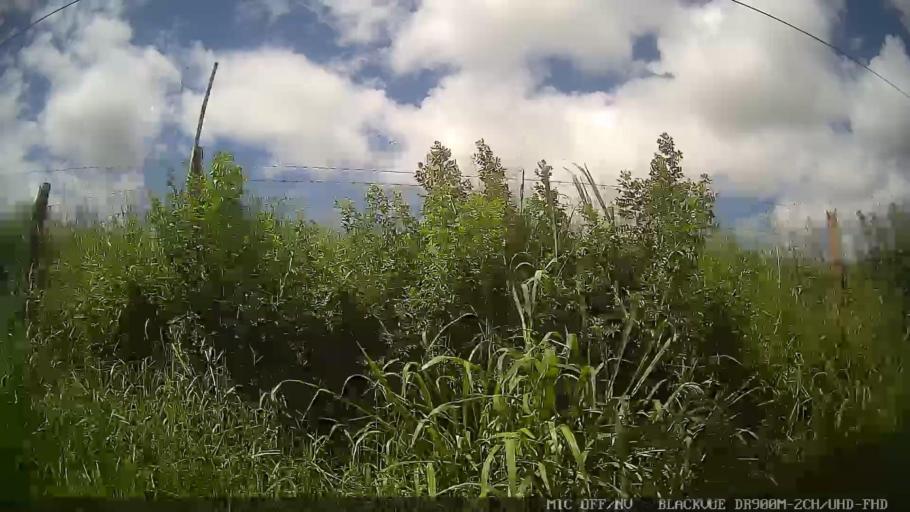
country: BR
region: Sao Paulo
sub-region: Braganca Paulista
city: Braganca Paulista
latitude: -22.8620
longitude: -46.6819
